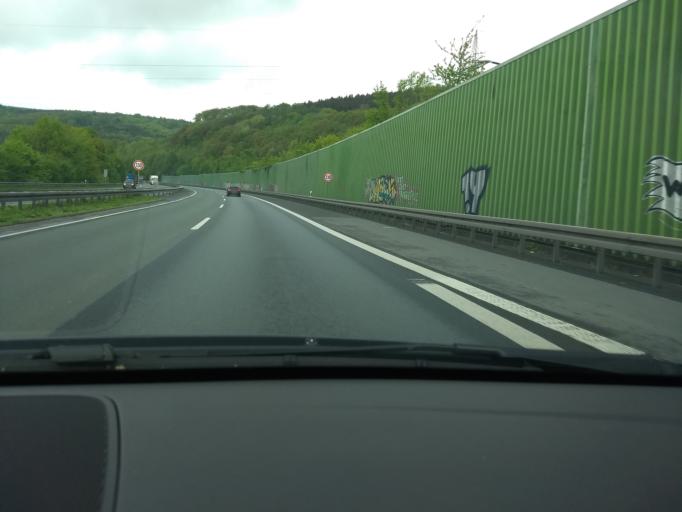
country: DE
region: North Rhine-Westphalia
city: Wickede
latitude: 51.4613
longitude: 7.9573
